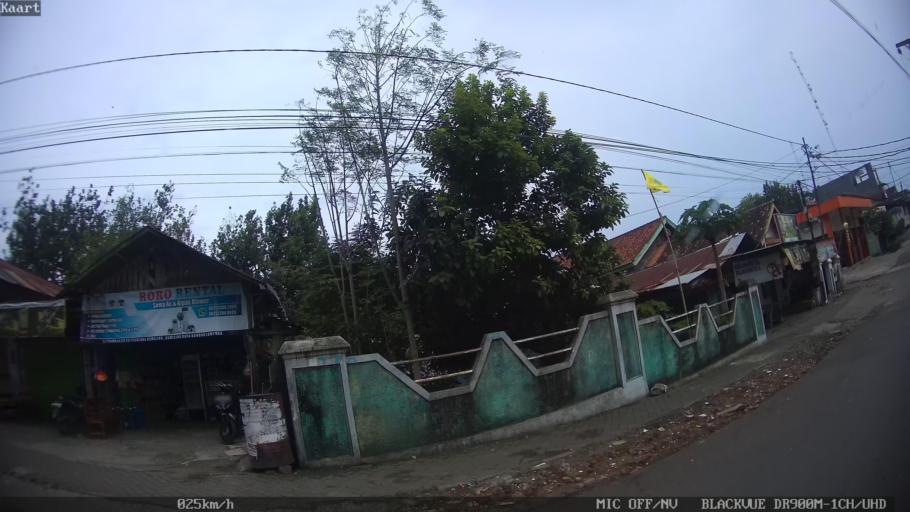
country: ID
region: Lampung
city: Kedaton
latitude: -5.3900
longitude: 105.2151
